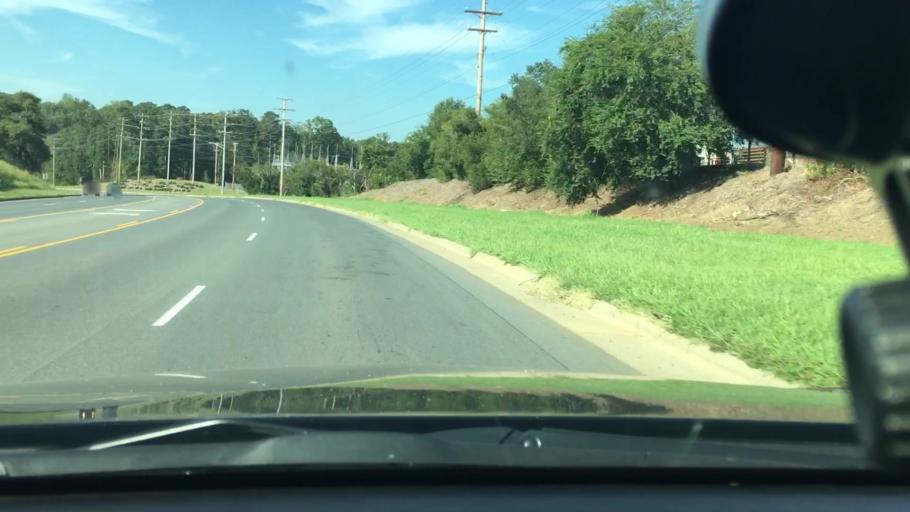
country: US
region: North Carolina
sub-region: Stanly County
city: Albemarle
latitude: 35.3399
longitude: -80.2144
